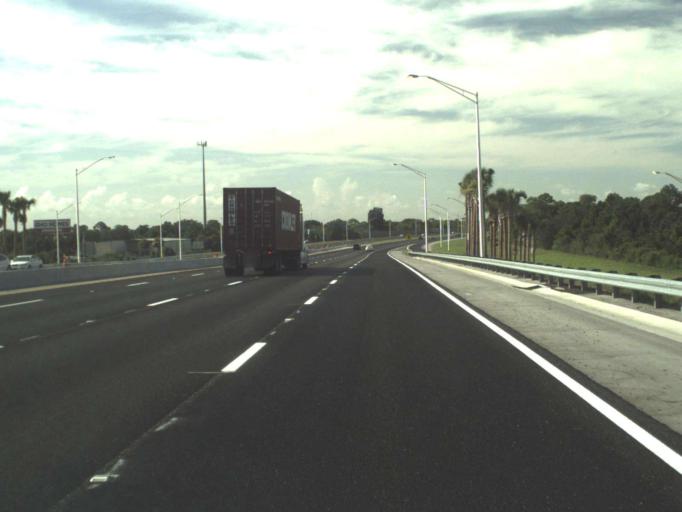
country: US
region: Florida
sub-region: Indian River County
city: West Vero Corridor
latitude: 27.6374
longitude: -80.5173
